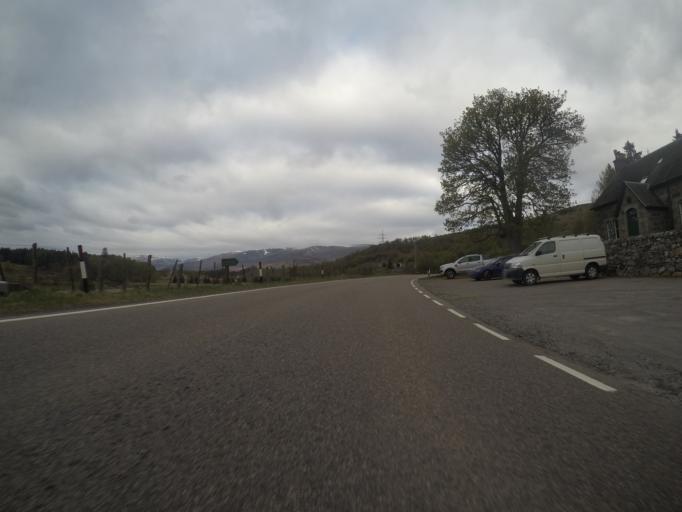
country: GB
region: Scotland
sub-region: Highland
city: Kingussie
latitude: 56.9744
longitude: -4.3860
